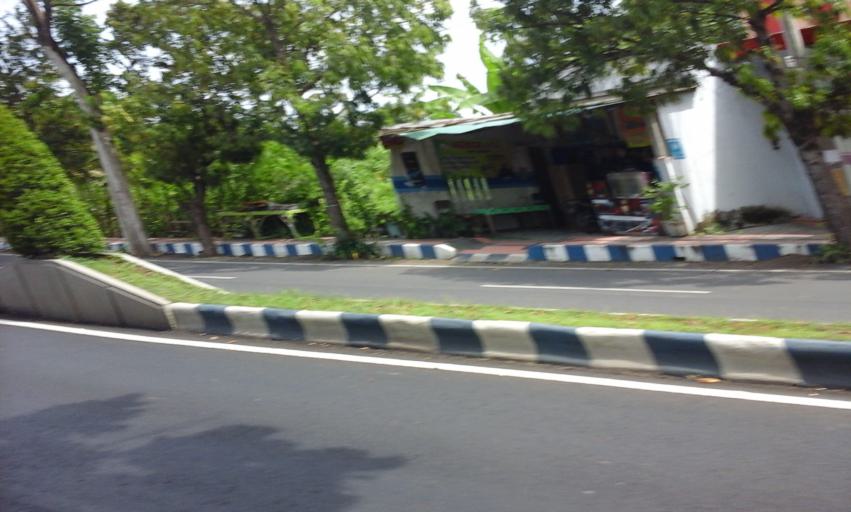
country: ID
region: East Java
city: Banyuwangi
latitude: -8.2334
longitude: 114.3522
